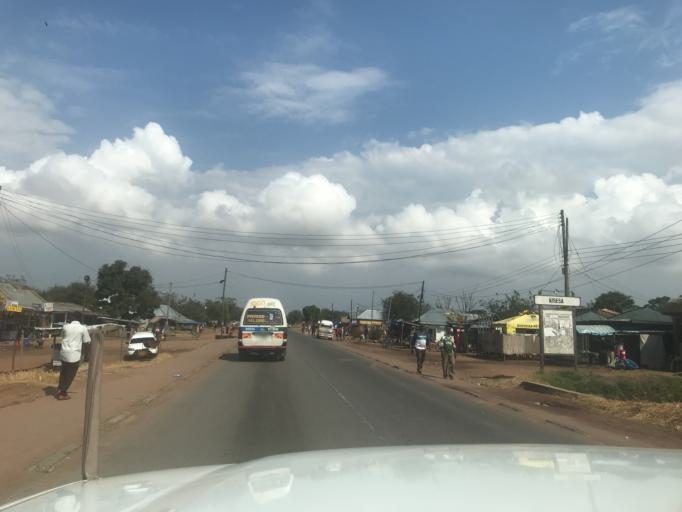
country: TZ
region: Mwanza
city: Usagara
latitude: -2.5554
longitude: 33.0446
